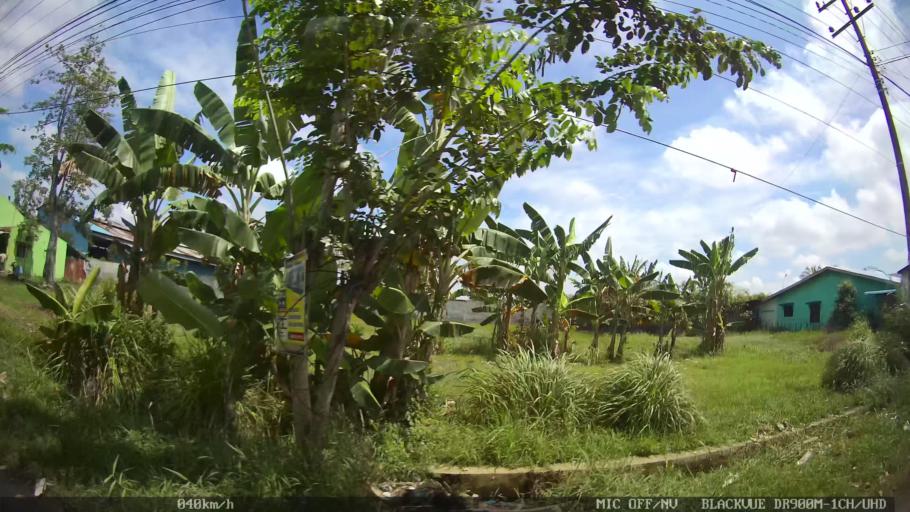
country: ID
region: North Sumatra
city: Percut
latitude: 3.6021
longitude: 98.7751
